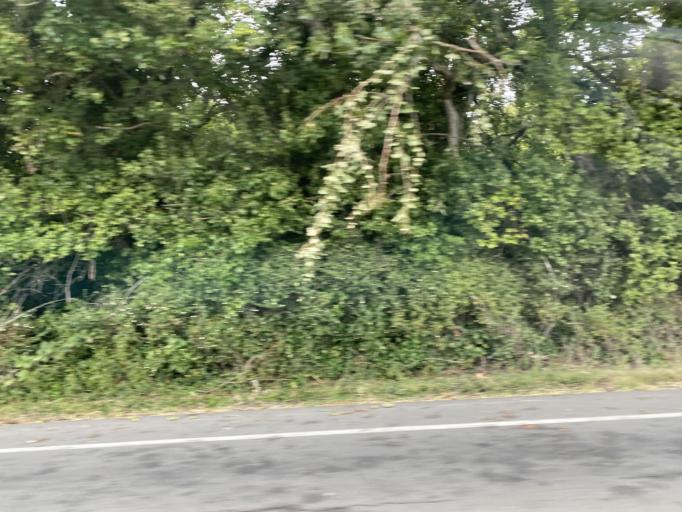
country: US
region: Washington
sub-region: Island County
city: Coupeville
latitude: 48.2070
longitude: -122.6931
